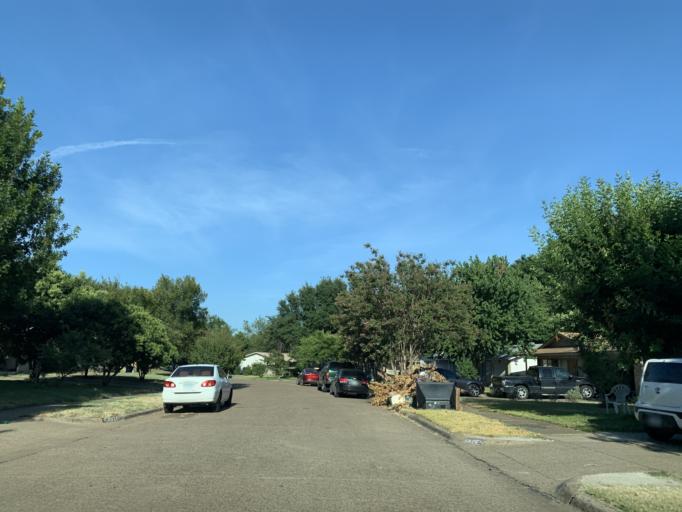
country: US
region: Texas
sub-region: Dallas County
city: Cockrell Hill
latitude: 32.7126
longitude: -96.8936
